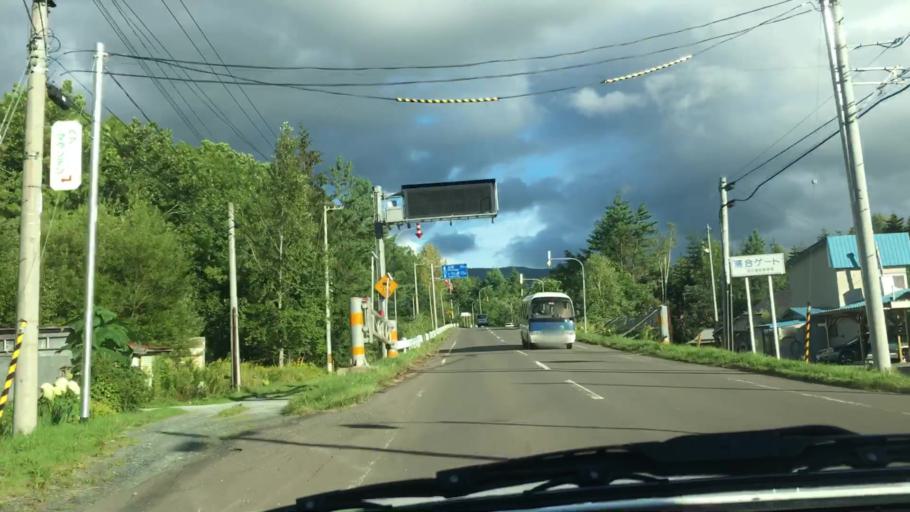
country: JP
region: Hokkaido
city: Shimo-furano
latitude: 43.1234
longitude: 142.6784
